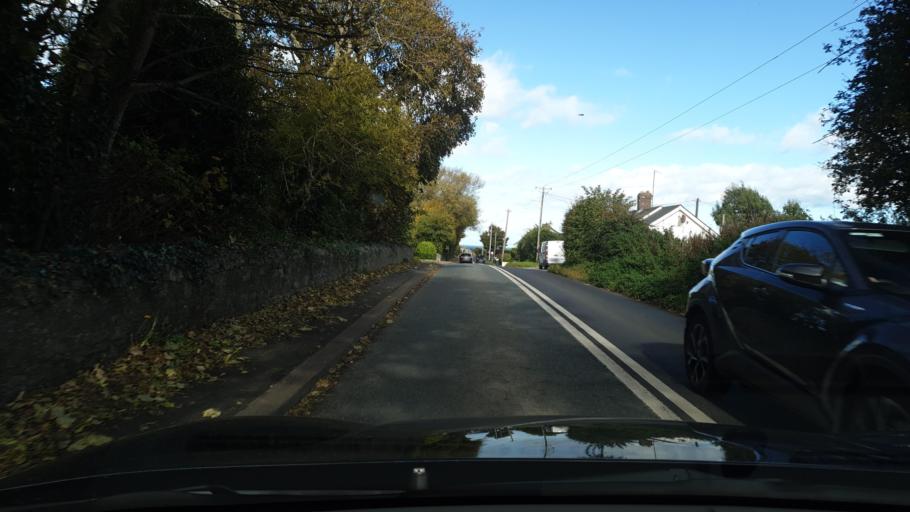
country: IE
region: Leinster
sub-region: Fingal County
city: Skerries
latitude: 53.5647
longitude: -6.1028
